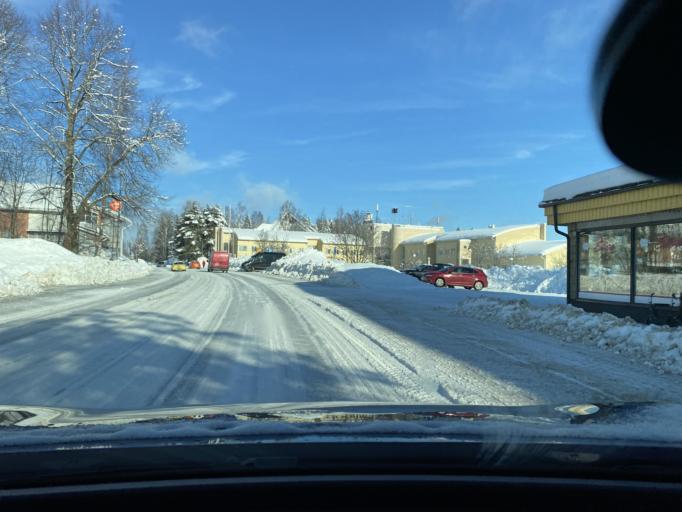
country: FI
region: Southern Savonia
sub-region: Mikkeli
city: Kangasniemi
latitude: 61.9888
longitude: 26.6433
